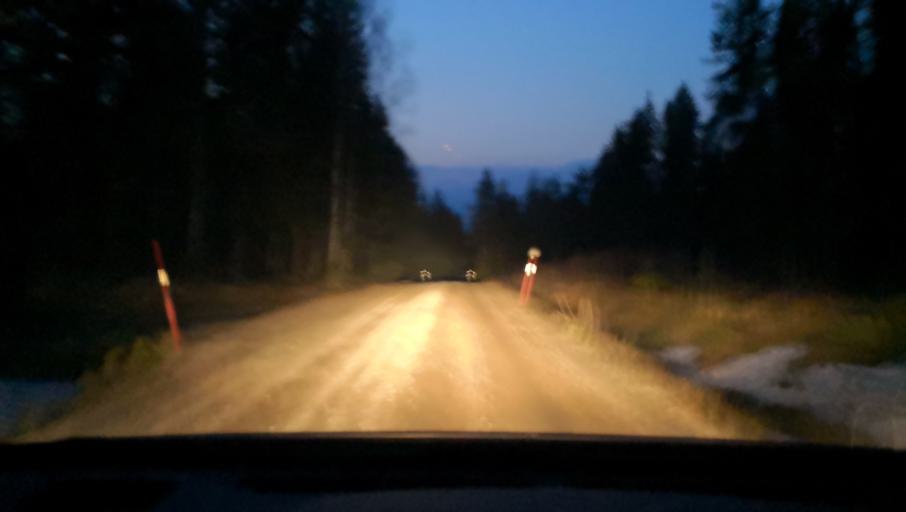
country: SE
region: OErebro
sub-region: Lindesbergs Kommun
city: Frovi
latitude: 59.6264
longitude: 15.4761
